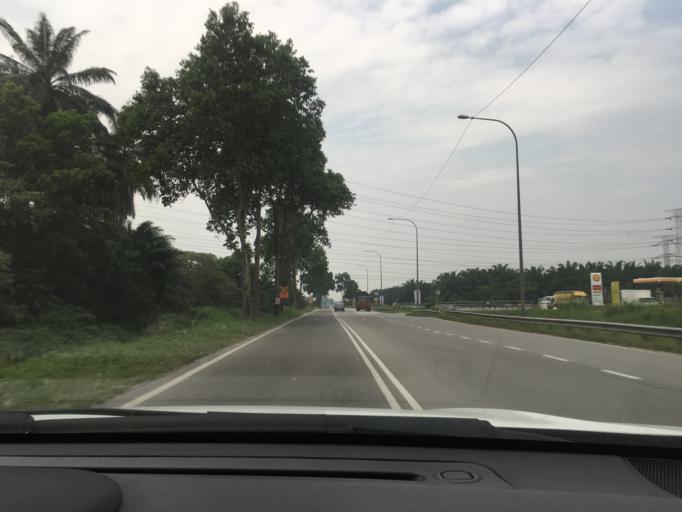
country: MY
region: Selangor
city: Klang
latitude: 3.1361
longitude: 101.4046
